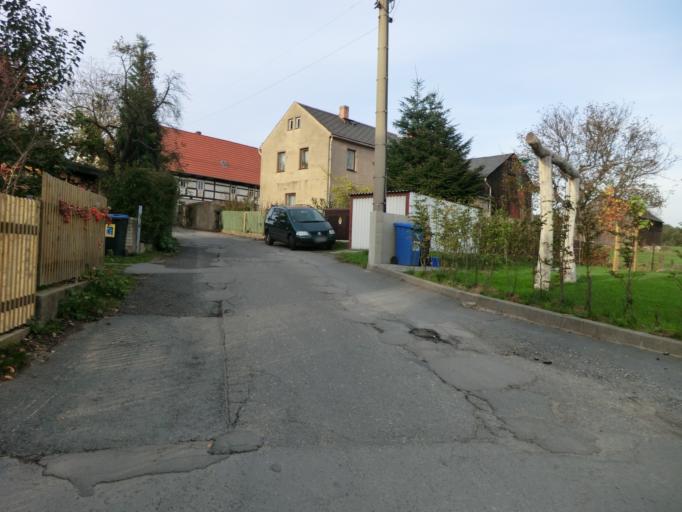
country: DE
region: Saxony
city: Heidenau
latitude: 51.0234
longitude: 13.8865
